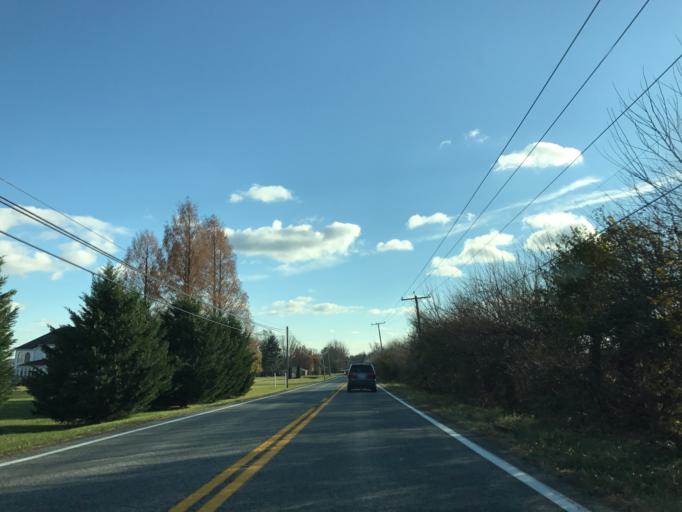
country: US
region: Maryland
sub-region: Harford County
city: Jarrettsville
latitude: 39.5690
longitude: -76.4993
